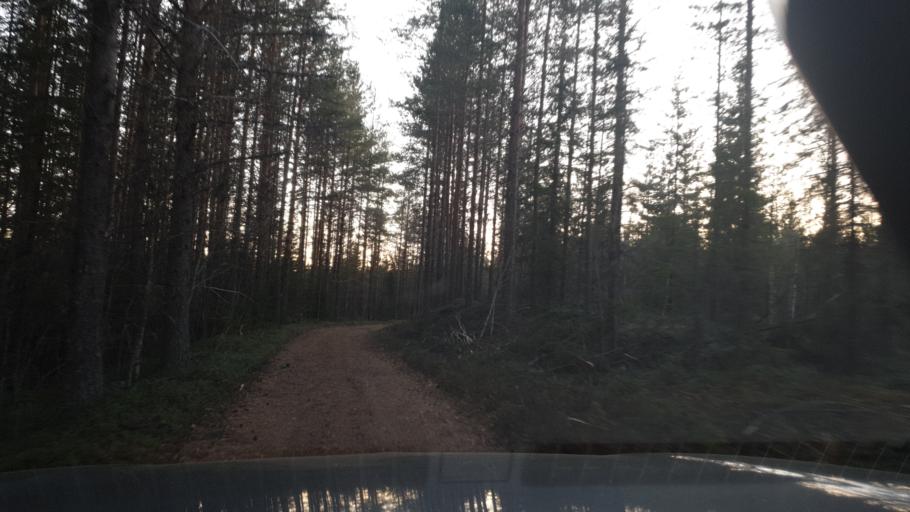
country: SE
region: Vaesternorrland
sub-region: Ange Kommun
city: Ange
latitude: 62.1889
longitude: 15.6059
